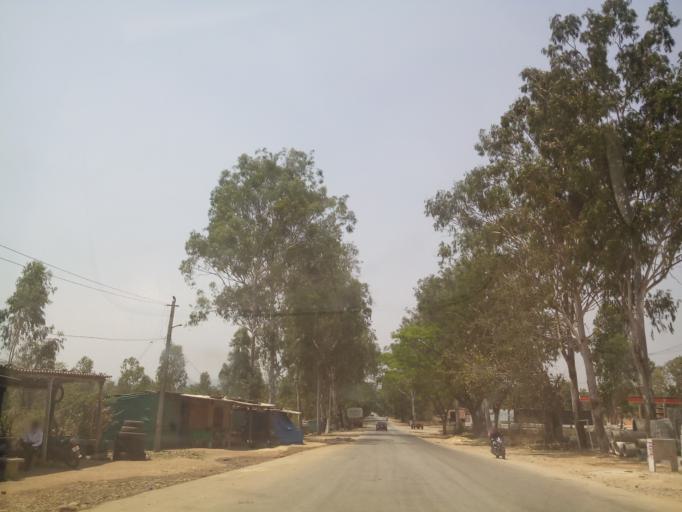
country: IN
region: Karnataka
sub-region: Hassan
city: Alur
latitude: 12.9592
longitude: 75.9842
